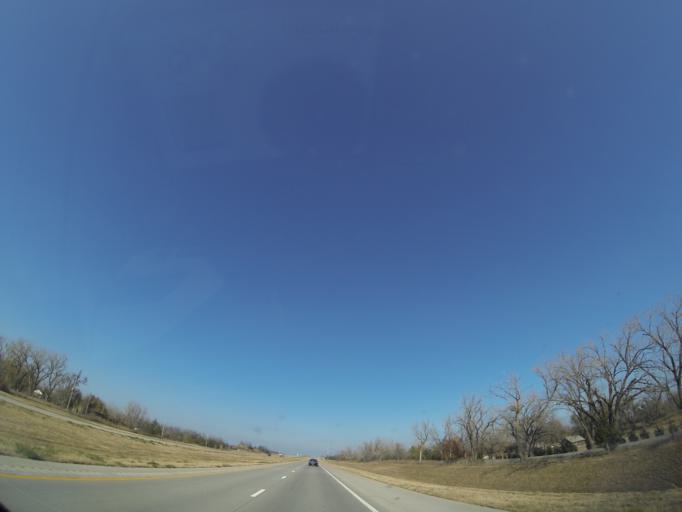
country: US
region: Kansas
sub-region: Reno County
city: Hutchinson
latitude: 38.1041
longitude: -97.8753
